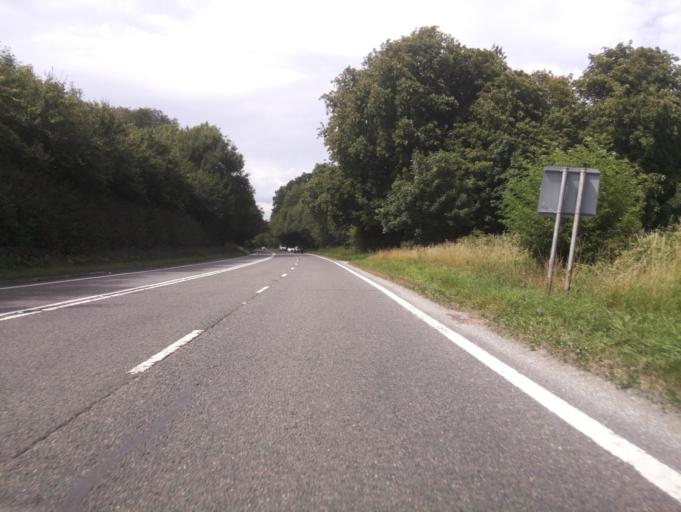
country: GB
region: England
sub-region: Somerset
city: Yeovil
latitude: 50.8552
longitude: -2.5865
